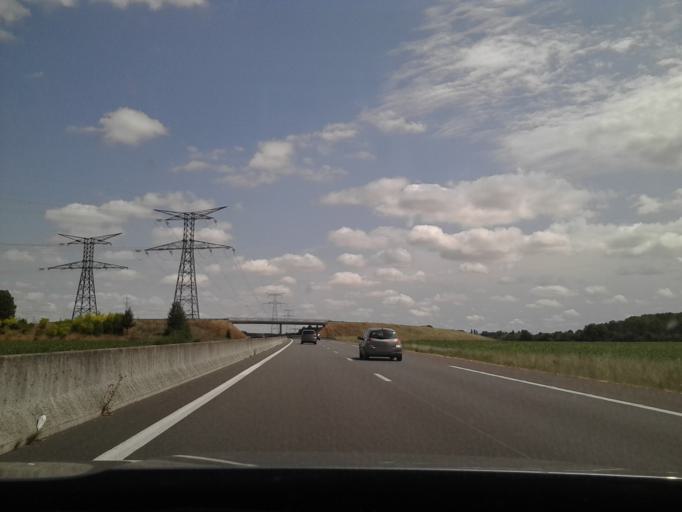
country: FR
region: Centre
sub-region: Departement d'Indre-et-Loire
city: Chanceaux-sur-Choisille
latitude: 47.4792
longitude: 0.7128
